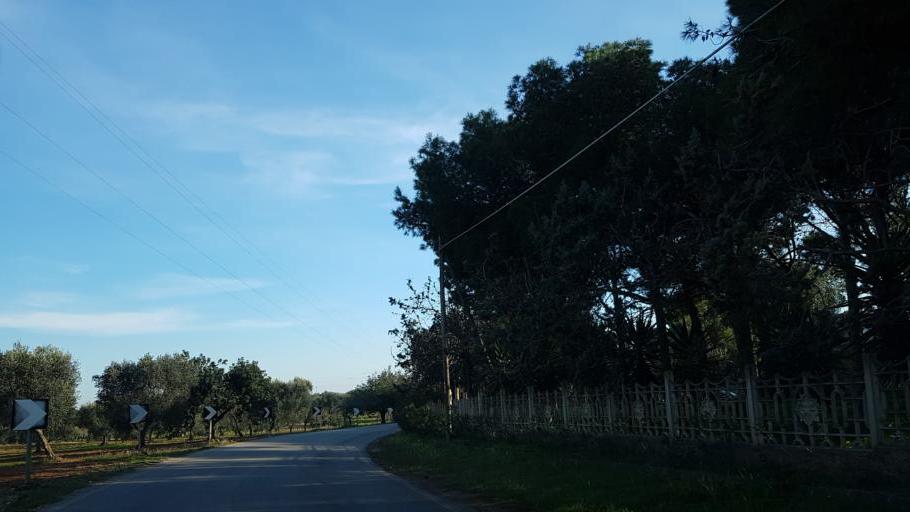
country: IT
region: Apulia
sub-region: Provincia di Brindisi
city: San Vito dei Normanni
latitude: 40.6777
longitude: 17.7753
